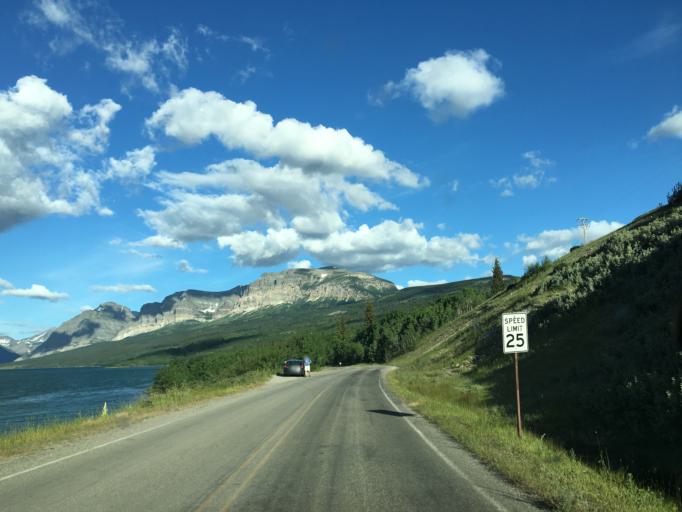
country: CA
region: Alberta
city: Cardston
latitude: 48.8299
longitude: -113.5252
